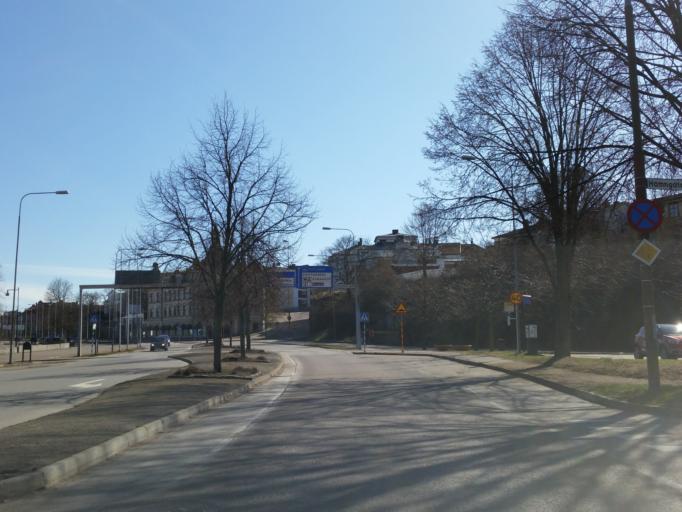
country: SE
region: Kalmar
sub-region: Oskarshamns Kommun
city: Oskarshamn
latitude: 57.2666
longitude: 16.4518
